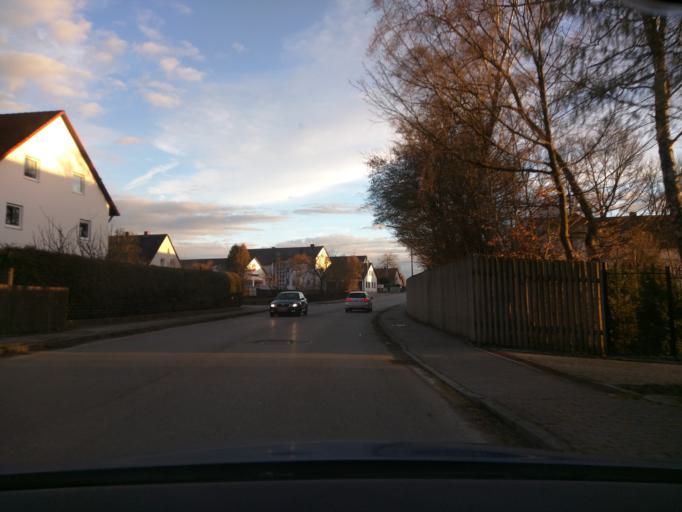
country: DE
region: Bavaria
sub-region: Upper Bavaria
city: Attenkirchen
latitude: 48.5040
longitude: 11.7587
